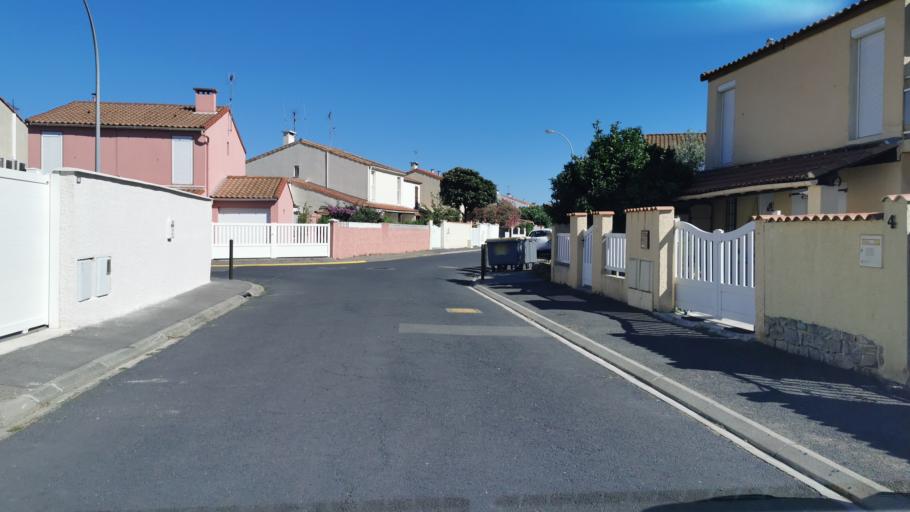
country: FR
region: Languedoc-Roussillon
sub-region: Departement de l'Aude
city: Narbonne
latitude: 43.1924
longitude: 3.0217
